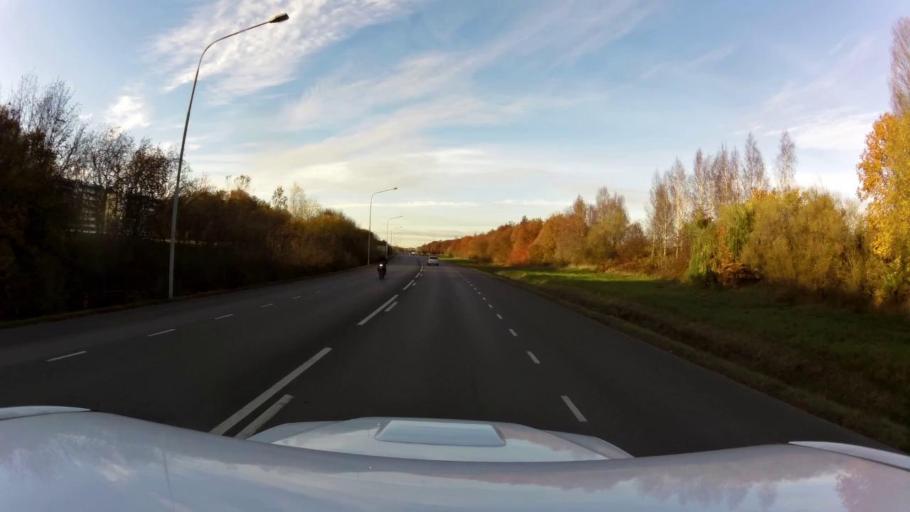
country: SE
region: OEstergoetland
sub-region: Linkopings Kommun
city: Sturefors
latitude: 58.3752
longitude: 15.6889
